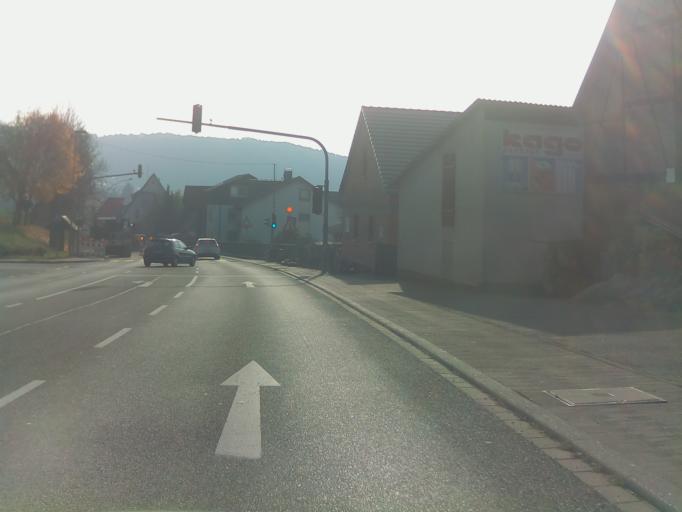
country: DE
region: Baden-Wuerttemberg
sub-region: Karlsruhe Region
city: Mosbach
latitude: 49.3883
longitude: 9.1931
